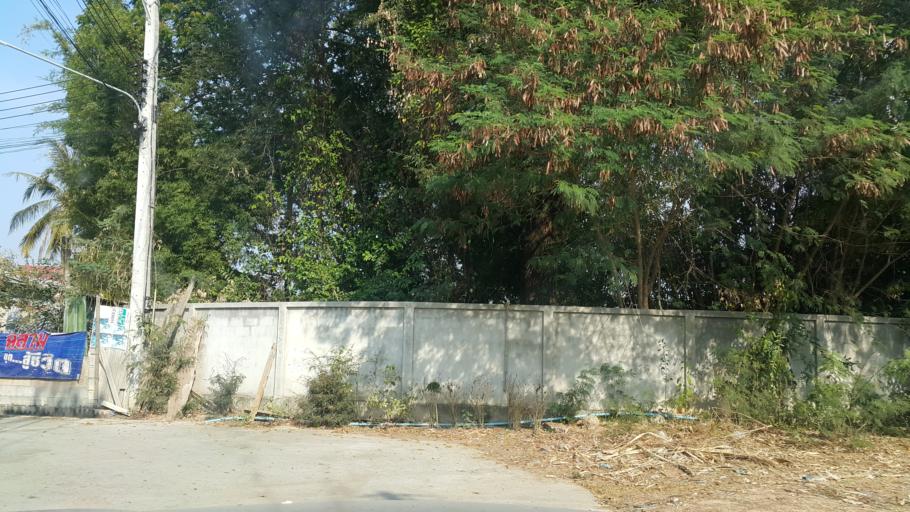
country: TH
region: Chiang Mai
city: San Sai
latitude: 18.8567
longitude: 99.0200
